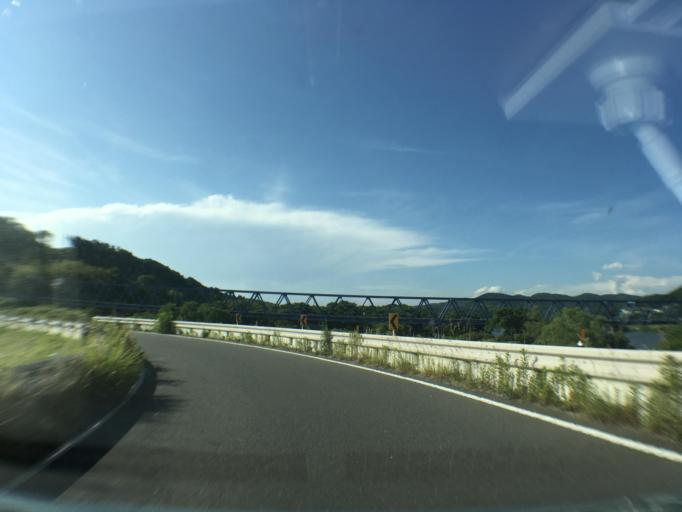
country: JP
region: Miyagi
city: Wakuya
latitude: 38.6074
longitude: 141.2945
